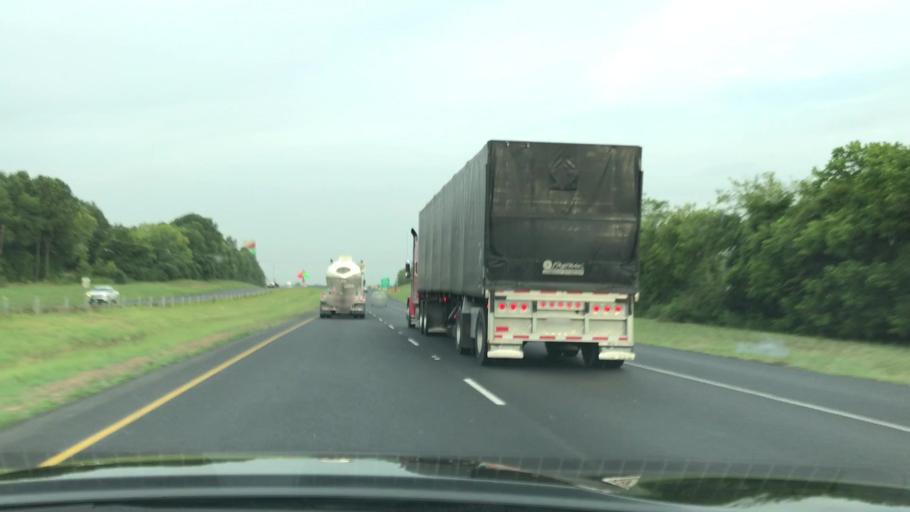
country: US
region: Louisiana
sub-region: Caddo Parish
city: Greenwood
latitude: 32.4462
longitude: -93.9715
